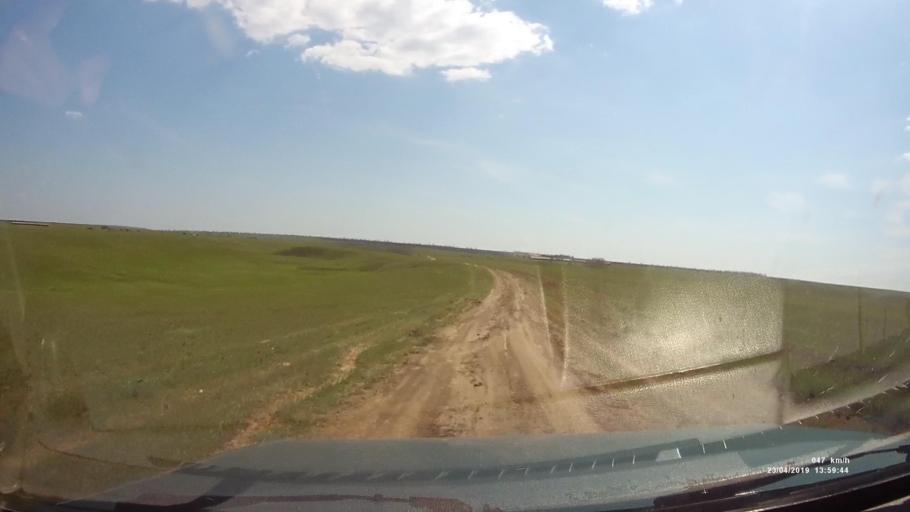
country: RU
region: Rostov
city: Remontnoye
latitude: 46.5645
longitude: 42.9471
